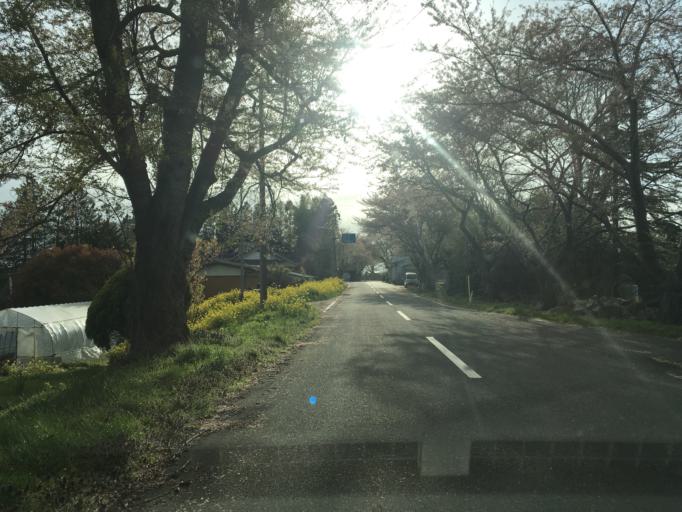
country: JP
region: Miyagi
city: Wakuya
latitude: 38.6460
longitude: 141.1741
